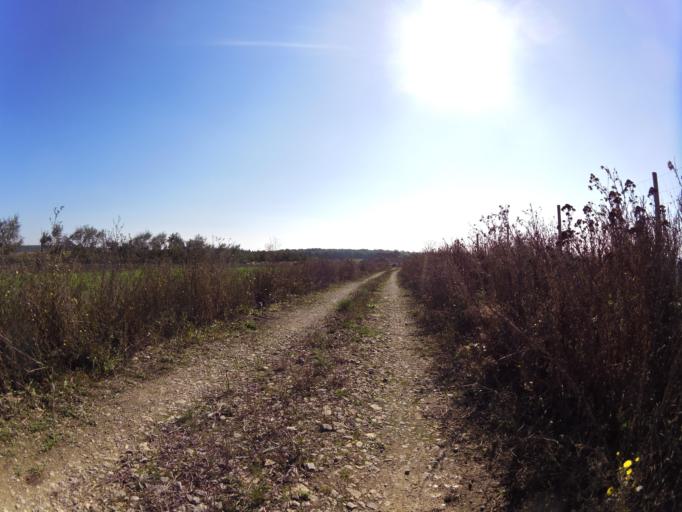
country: DE
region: Bavaria
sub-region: Regierungsbezirk Unterfranken
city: Sommerhausen
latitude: 49.6893
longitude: 10.0394
